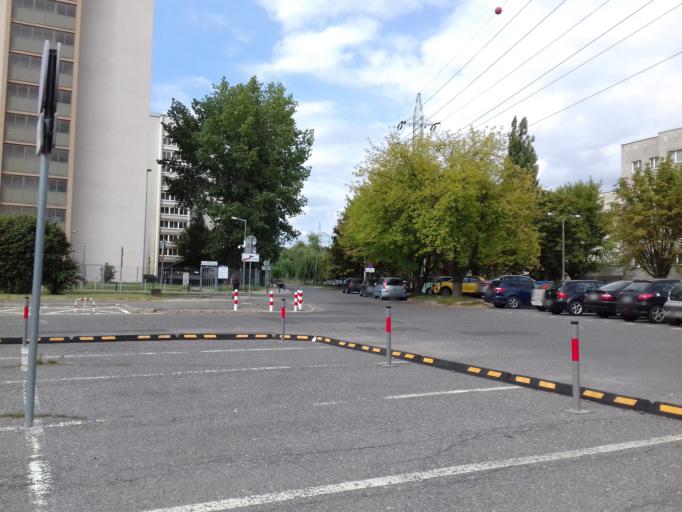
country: PL
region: Lesser Poland Voivodeship
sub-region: Krakow
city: Krakow
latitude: 50.0840
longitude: 19.9966
